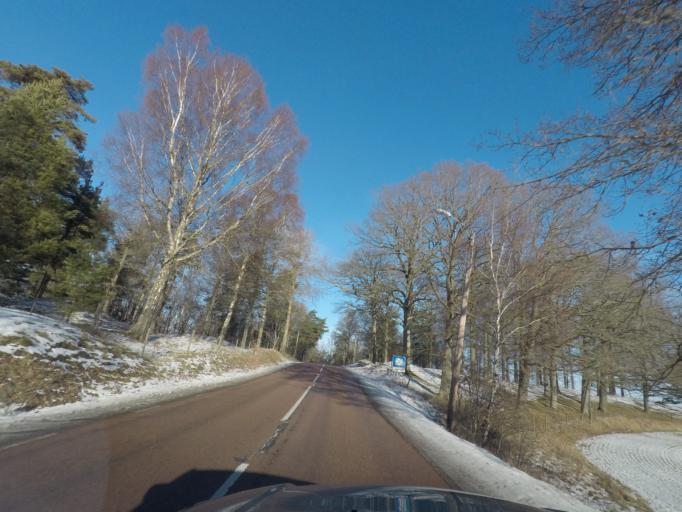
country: SE
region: Soedermanland
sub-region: Eskilstuna Kommun
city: Kvicksund
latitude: 59.4387
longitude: 16.3396
